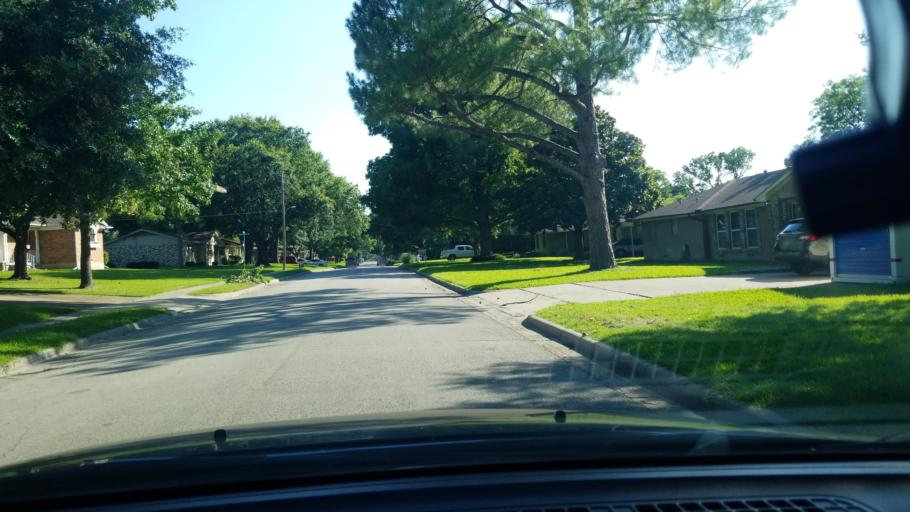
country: US
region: Texas
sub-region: Dallas County
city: Mesquite
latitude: 32.7547
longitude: -96.5991
